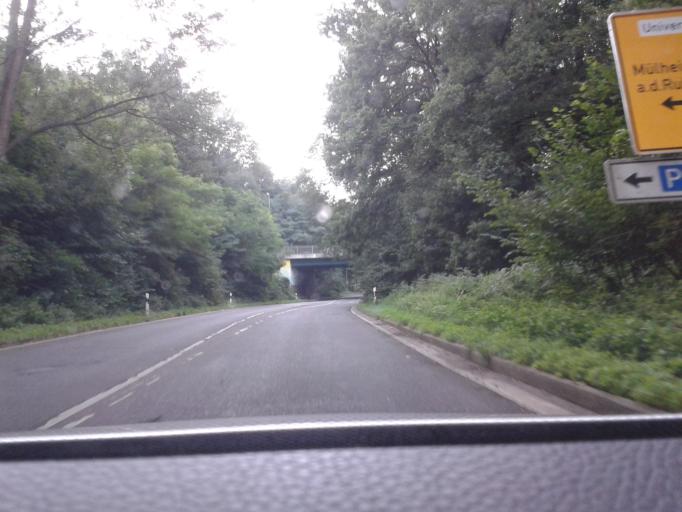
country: DE
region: North Rhine-Westphalia
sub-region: Regierungsbezirk Dusseldorf
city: Duisburg
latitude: 51.4341
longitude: 6.8103
